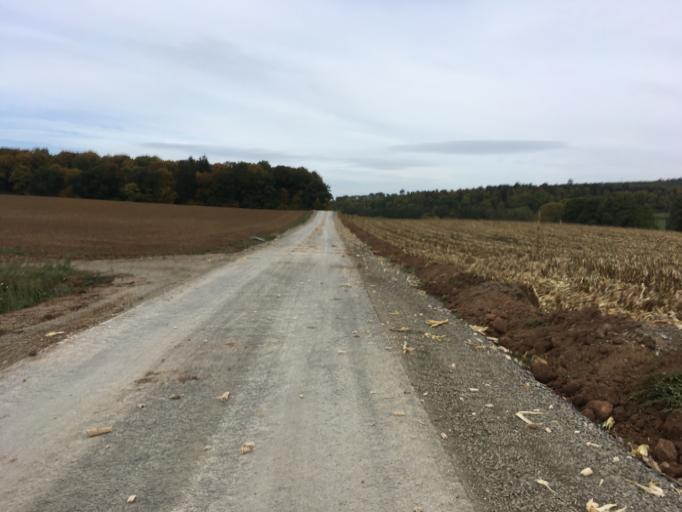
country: DE
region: Baden-Wuerttemberg
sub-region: Karlsruhe Region
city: Buchen
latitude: 49.4880
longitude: 9.3151
